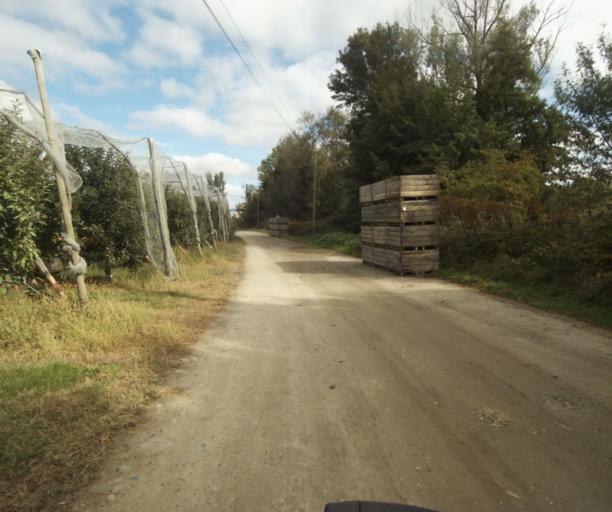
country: FR
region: Midi-Pyrenees
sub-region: Departement du Tarn-et-Garonne
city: Montech
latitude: 43.9502
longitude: 1.1878
